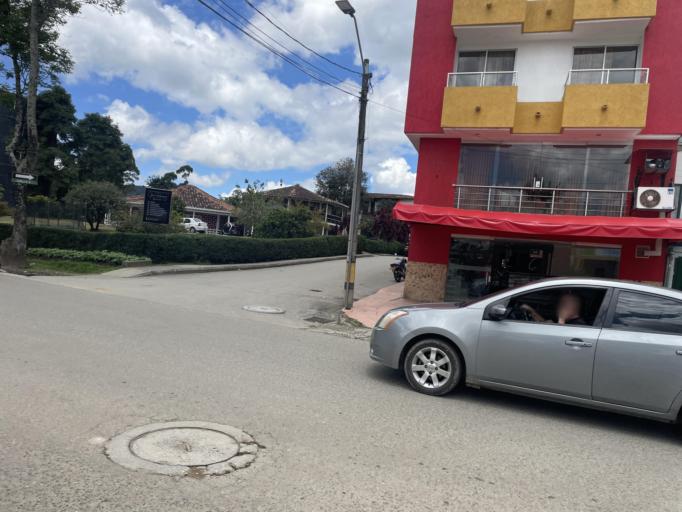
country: CO
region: Antioquia
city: La Ceja
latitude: 6.0219
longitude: -75.4334
